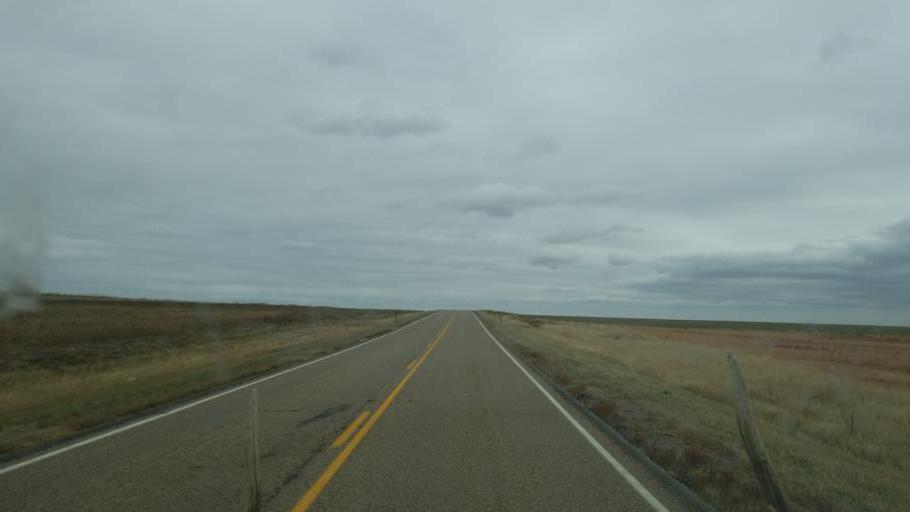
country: US
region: Colorado
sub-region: Cheyenne County
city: Cheyenne Wells
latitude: 38.8477
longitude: -102.1481
